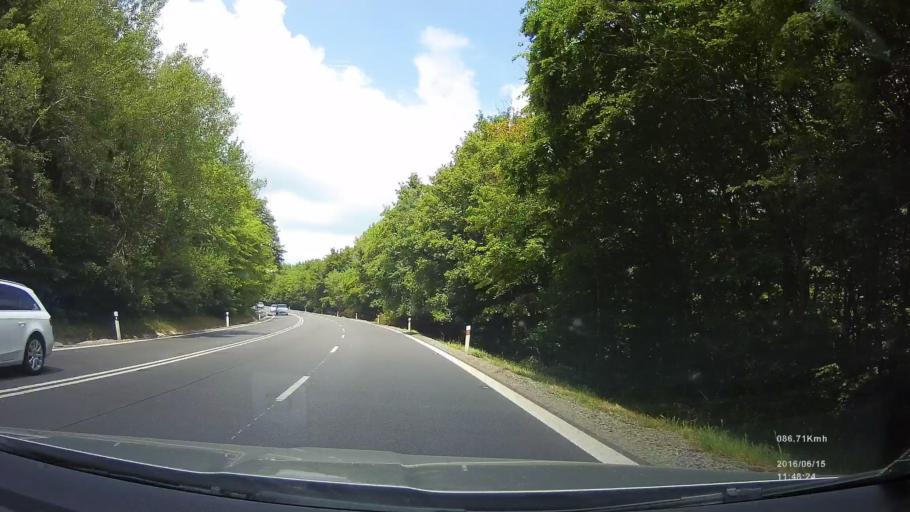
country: SK
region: Kosicky
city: Kosice
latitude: 48.7332
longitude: 21.3212
